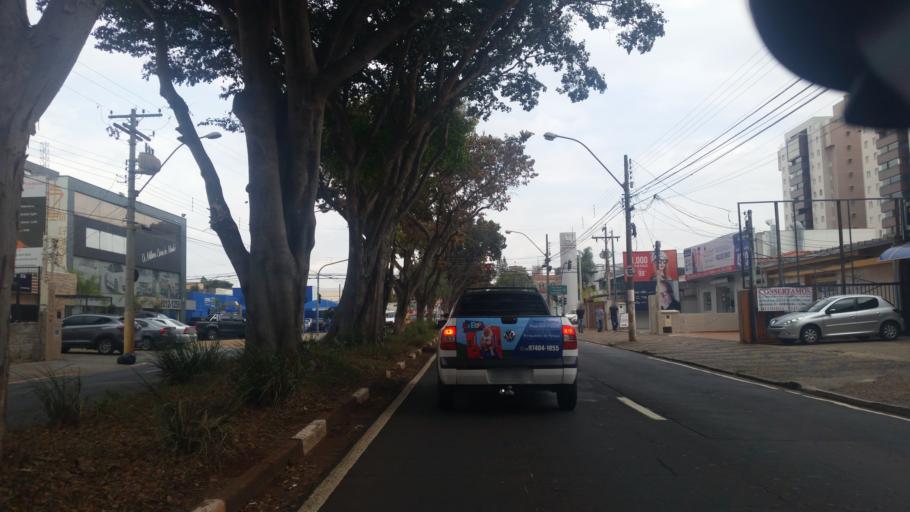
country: BR
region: Sao Paulo
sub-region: Campinas
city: Campinas
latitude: -22.8835
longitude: -47.0737
